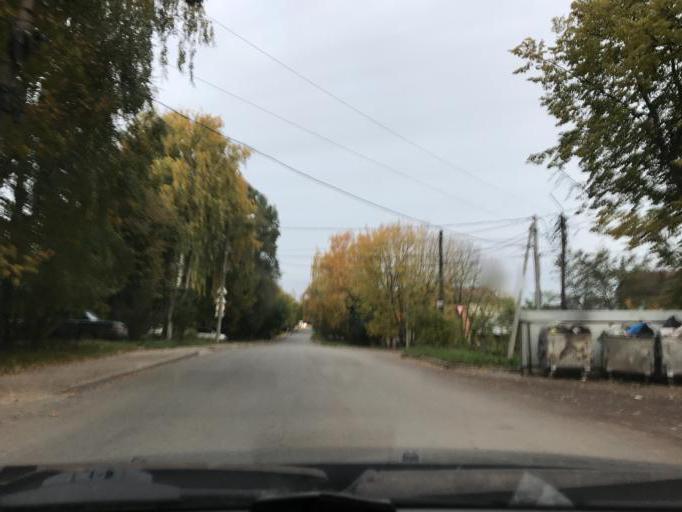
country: RU
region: Kaluga
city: Kaluga
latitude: 54.5360
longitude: 36.2473
